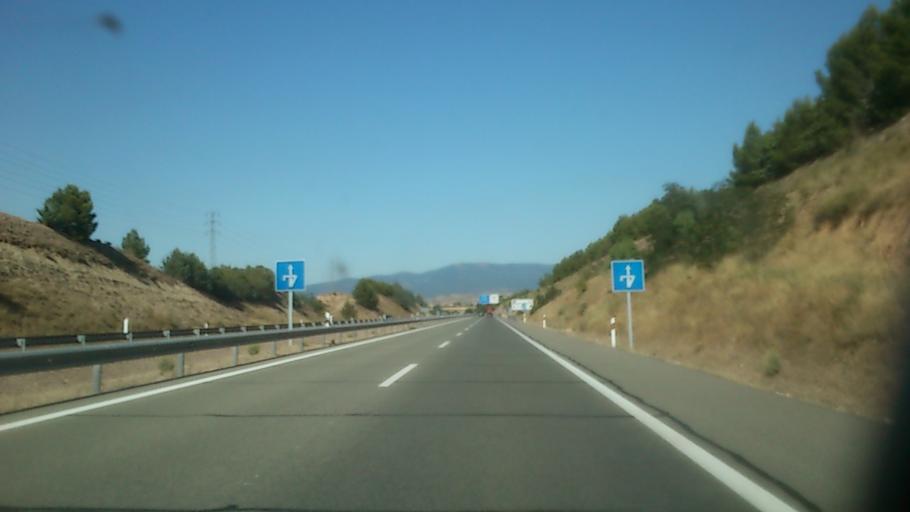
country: ES
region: Aragon
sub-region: Provincia de Zaragoza
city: Terrer
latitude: 41.3225
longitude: -1.6779
